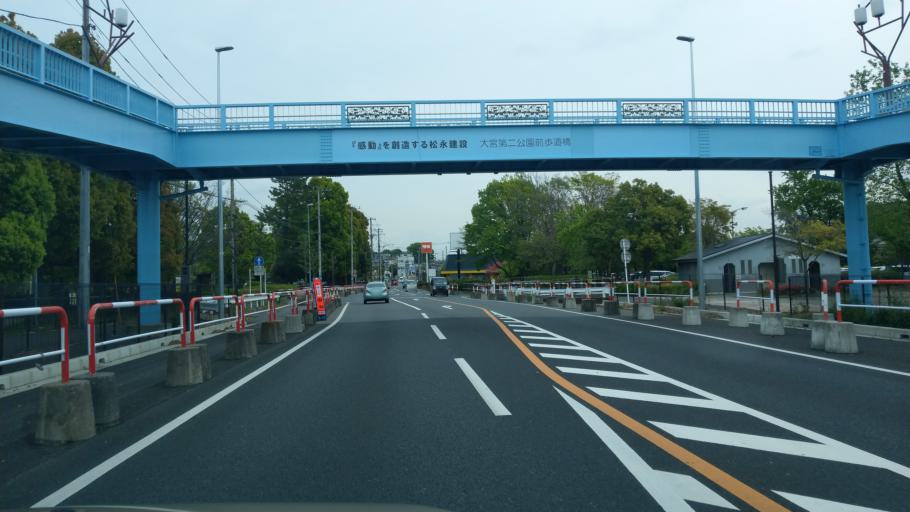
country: JP
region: Saitama
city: Saitama
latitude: 35.9162
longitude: 139.6419
